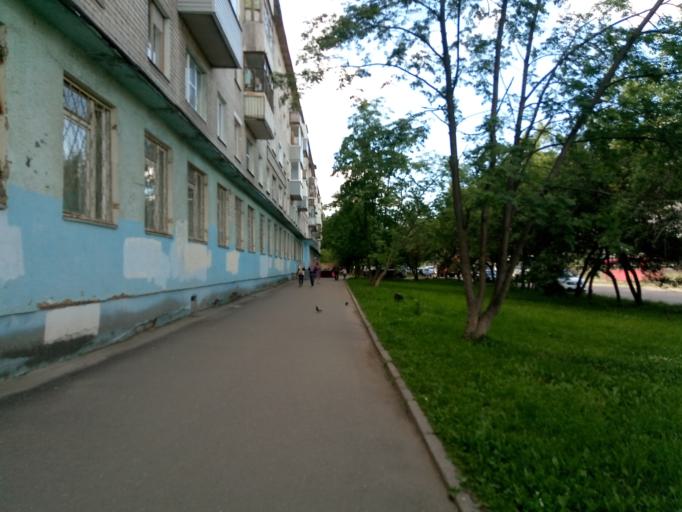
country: RU
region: Jaroslavl
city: Yaroslavl
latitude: 57.6514
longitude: 39.9469
